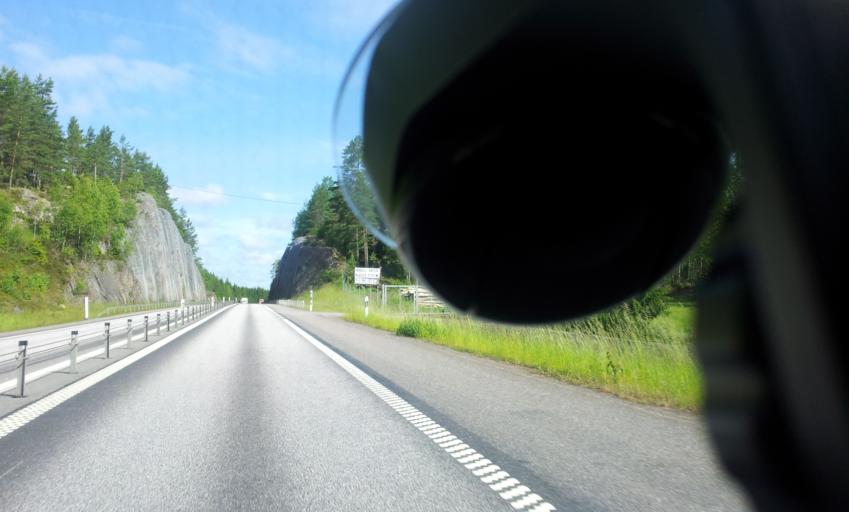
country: SE
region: OEstergoetland
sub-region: Valdemarsviks Kommun
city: Gusum
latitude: 58.2520
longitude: 16.5321
